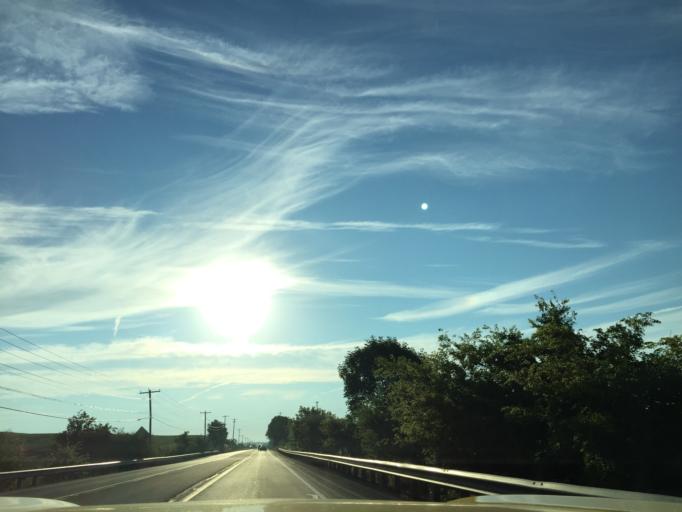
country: US
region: Pennsylvania
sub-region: Berks County
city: Topton
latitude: 40.5400
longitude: -75.7155
